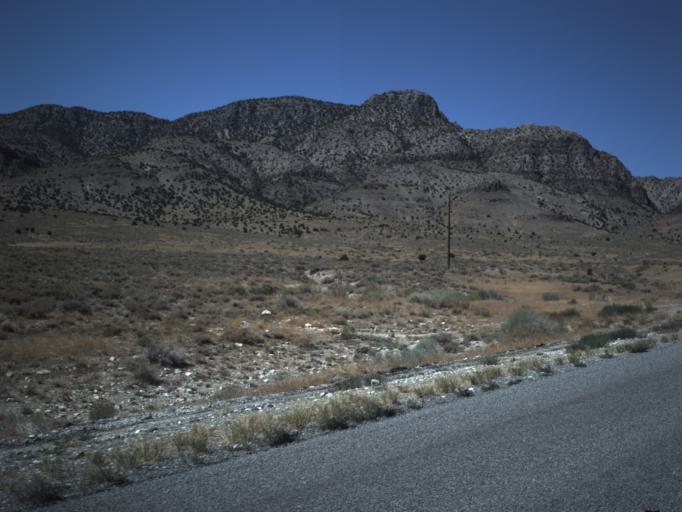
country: US
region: Utah
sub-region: Beaver County
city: Milford
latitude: 39.0870
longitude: -113.5388
